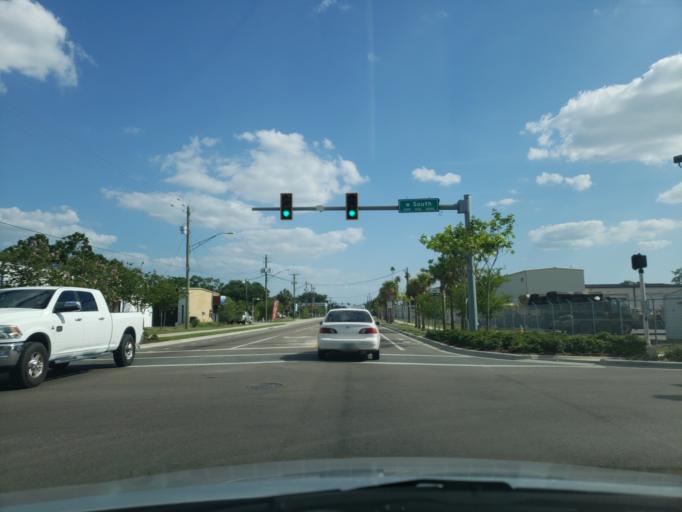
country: US
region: Florida
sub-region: Hillsborough County
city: Egypt Lake-Leto
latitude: 27.9915
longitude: -82.5135
